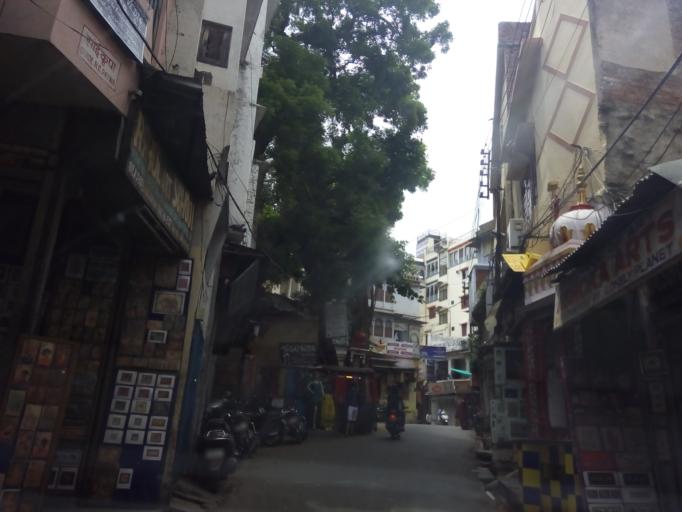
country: IN
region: Rajasthan
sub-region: Udaipur
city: Udaipur
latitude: 24.5800
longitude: 73.6839
